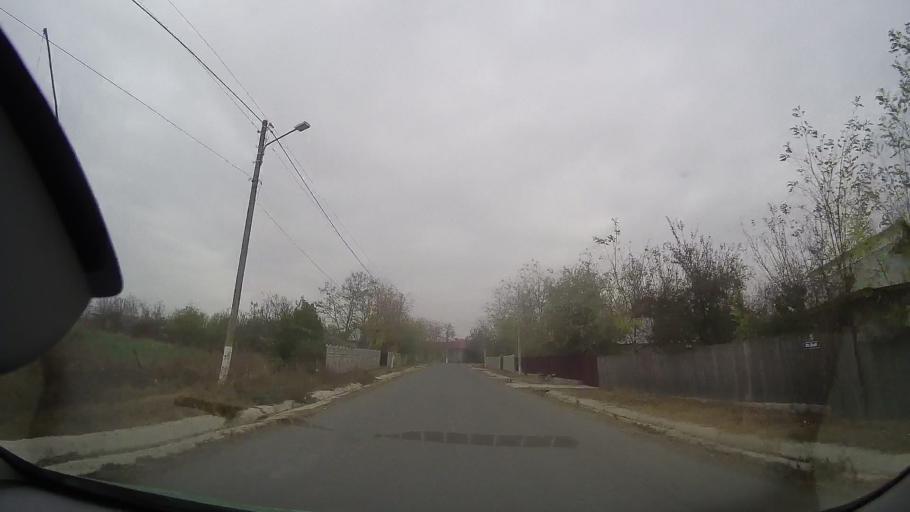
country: RO
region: Braila
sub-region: Comuna Ciocile
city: Ciocile
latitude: 44.8038
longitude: 27.2725
